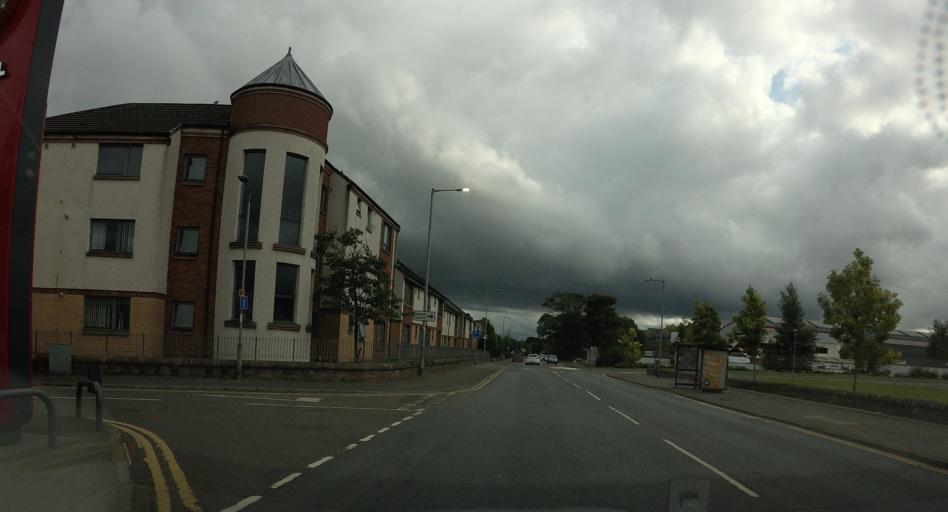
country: GB
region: Scotland
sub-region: Clackmannanshire
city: Alloa
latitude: 56.1239
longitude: -3.7815
